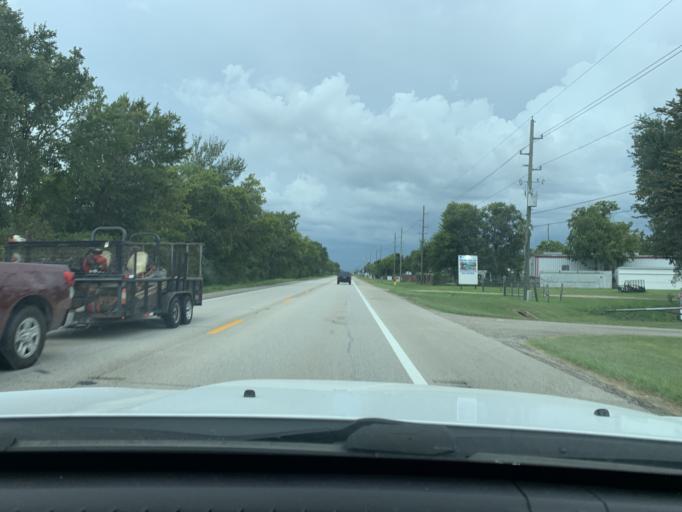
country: US
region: Texas
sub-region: Fort Bend County
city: Greatwood
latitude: 29.5393
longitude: -95.7156
